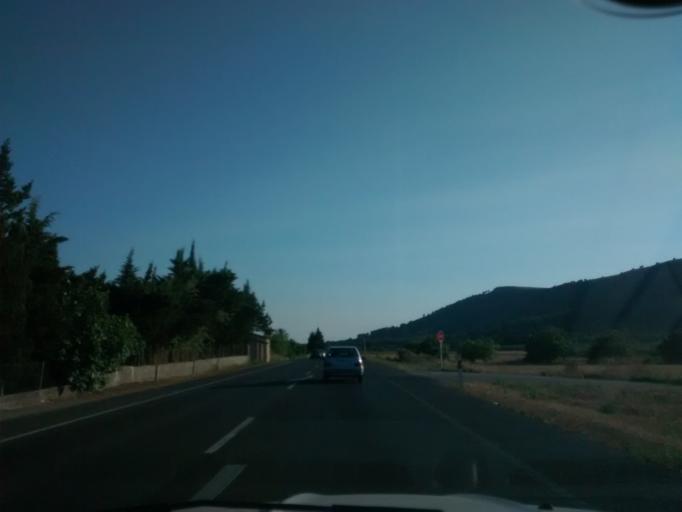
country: ES
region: Balearic Islands
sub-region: Illes Balears
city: Alcudia
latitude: 39.8319
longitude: 3.0651
